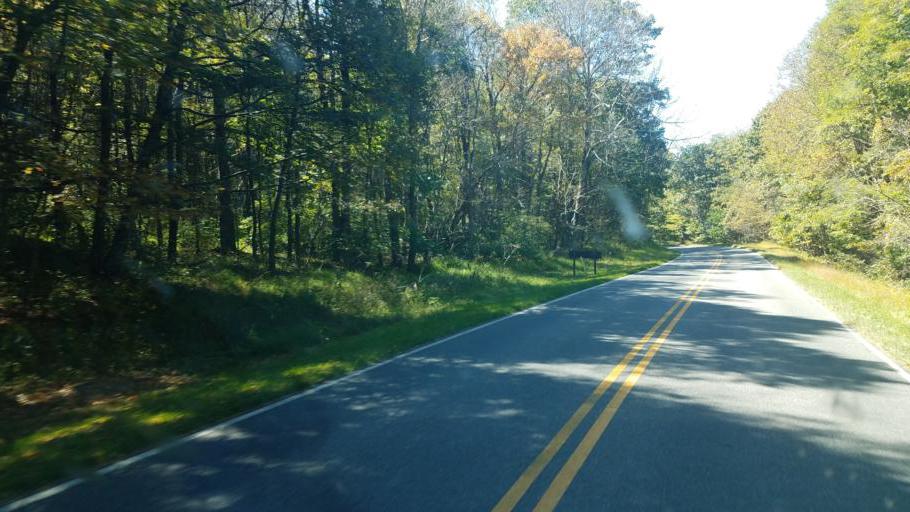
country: US
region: Virginia
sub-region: Rockingham County
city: Elkton
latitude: 38.3831
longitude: -78.5192
